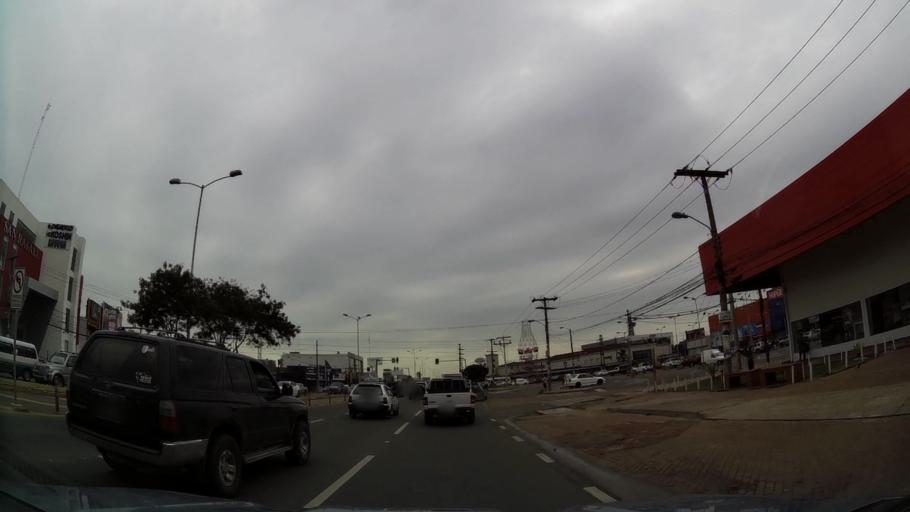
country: BO
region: Santa Cruz
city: Santa Cruz de la Sierra
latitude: -17.7623
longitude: -63.1802
